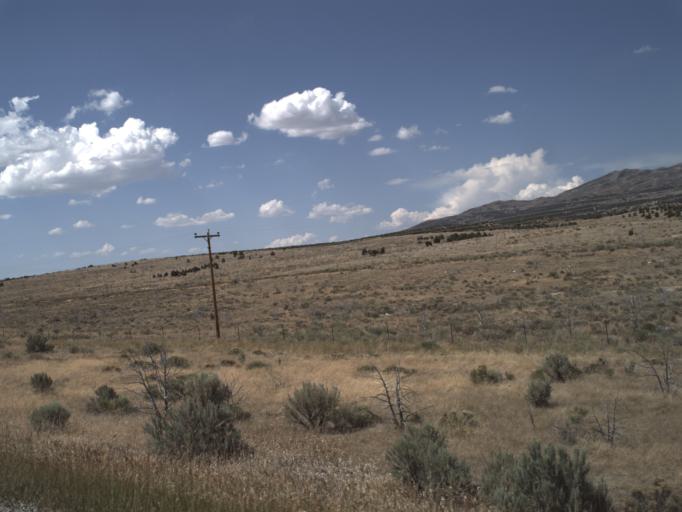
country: US
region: Idaho
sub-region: Minidoka County
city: Rupert
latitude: 41.9793
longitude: -113.1654
